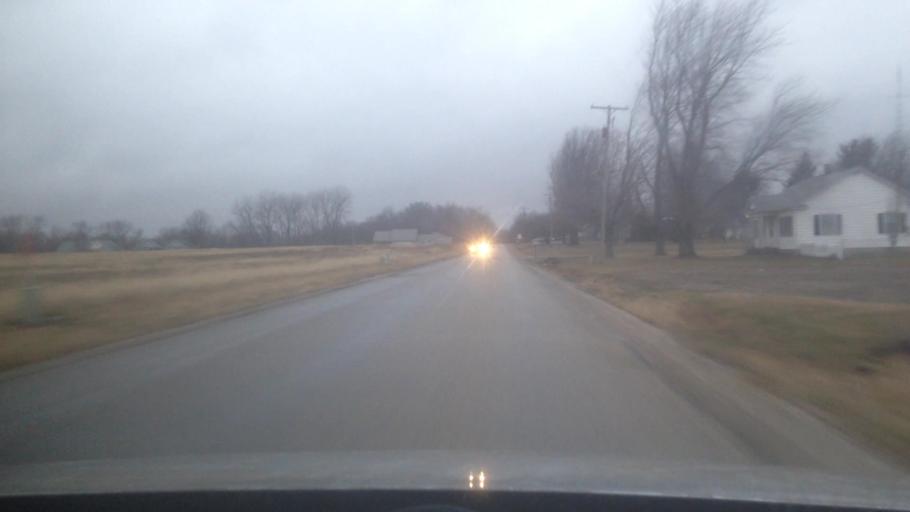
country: US
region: Illinois
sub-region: Christian County
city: Pana
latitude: 39.3829
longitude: -89.0593
